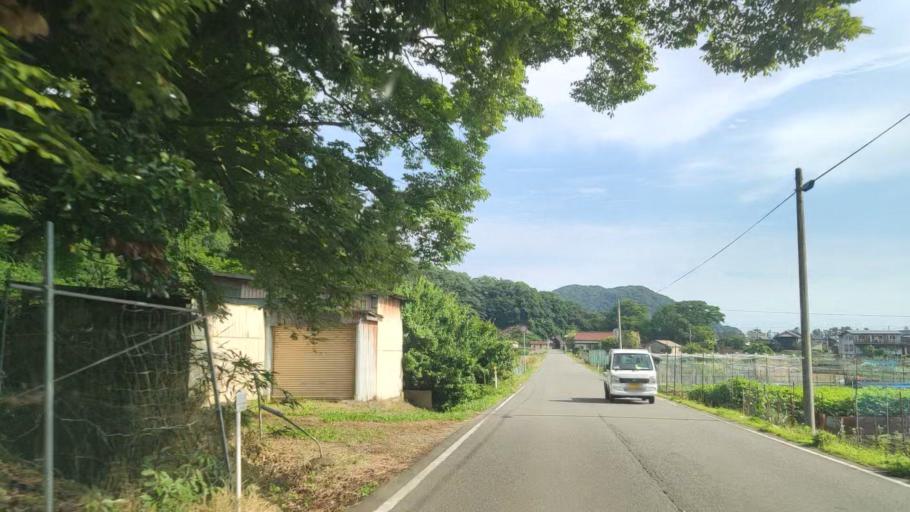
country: JP
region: Hyogo
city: Toyooka
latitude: 35.6362
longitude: 134.8365
